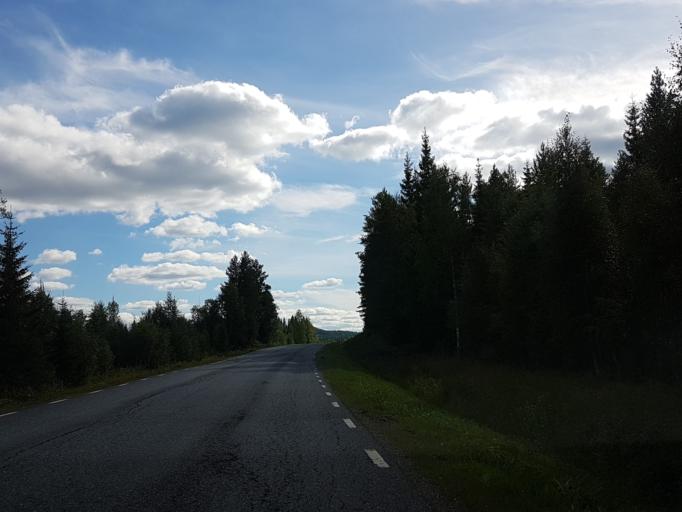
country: SE
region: Vaesterbotten
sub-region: Skelleftea Kommun
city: Burtraesk
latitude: 64.3093
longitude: 20.5311
